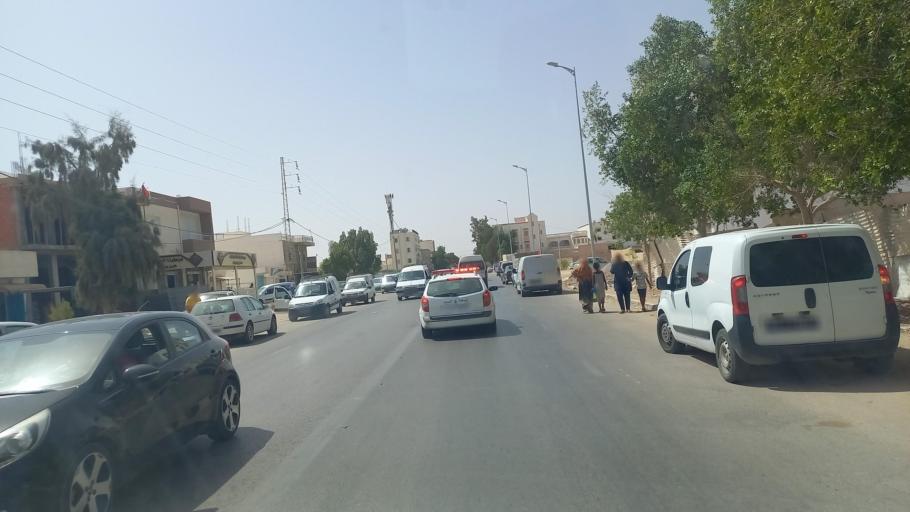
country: TN
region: Madanin
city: Medenine
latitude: 33.3304
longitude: 10.4852
